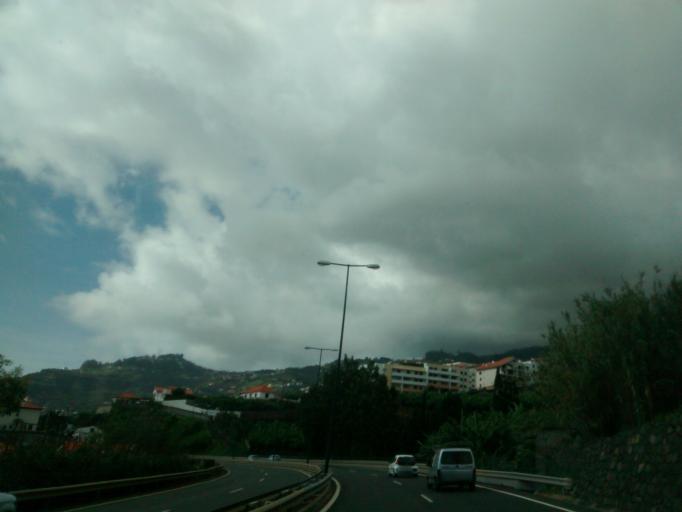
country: PT
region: Madeira
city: Camara de Lobos
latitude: 32.6583
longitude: -16.9703
